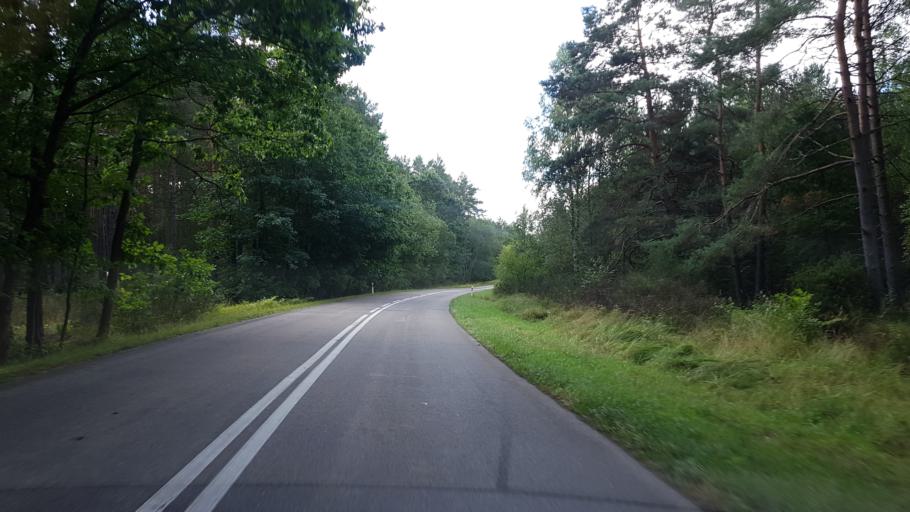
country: PL
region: West Pomeranian Voivodeship
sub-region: Powiat bialogardzki
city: Tychowo
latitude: 54.0536
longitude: 16.3017
